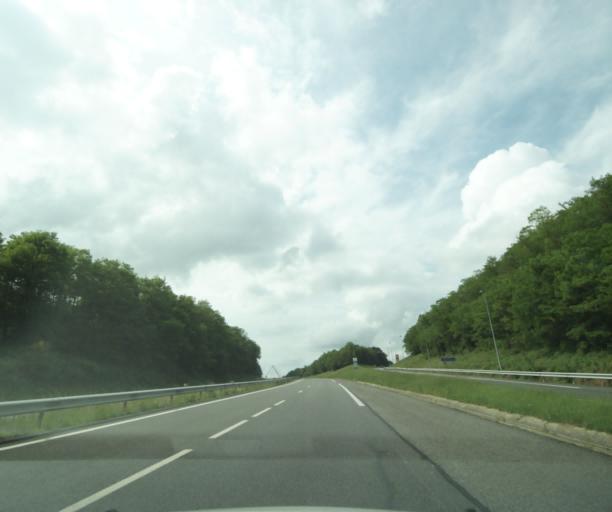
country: FR
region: Centre
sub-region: Departement du Cher
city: Orval
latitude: 46.7486
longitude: 2.4229
